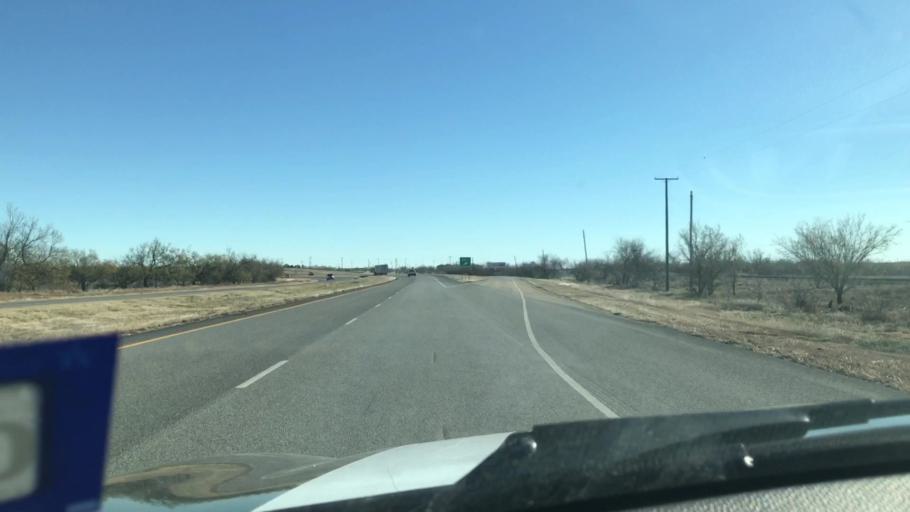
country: US
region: Texas
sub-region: Scurry County
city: Snyder
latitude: 32.7987
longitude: -100.9656
